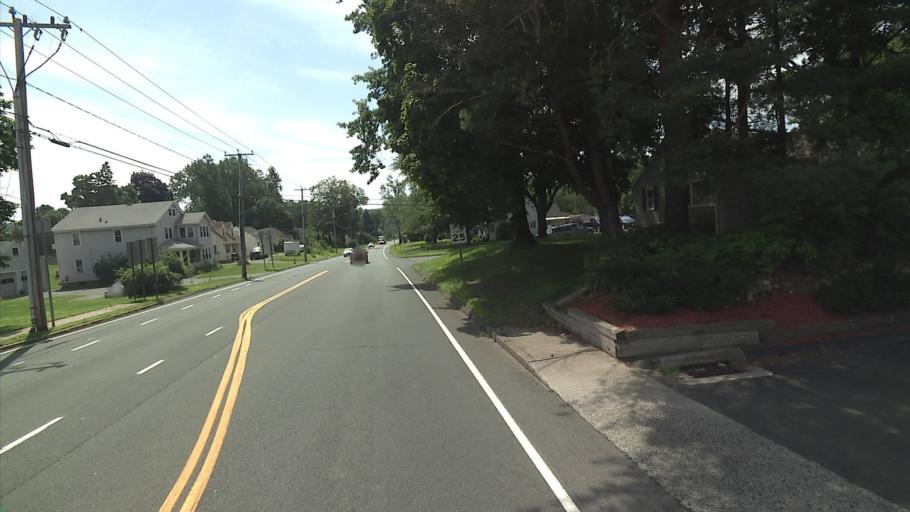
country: US
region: Connecticut
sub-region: Tolland County
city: Rockville
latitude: 41.8589
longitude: -72.4321
